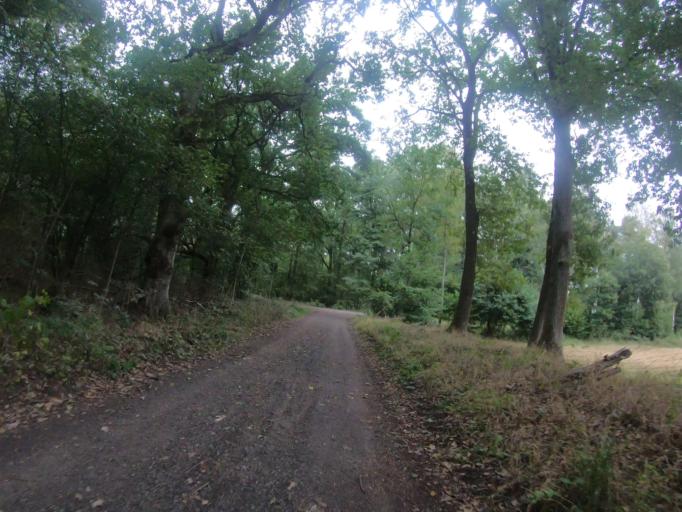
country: DE
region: Lower Saxony
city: Ribbesbuttel
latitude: 52.4539
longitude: 10.5243
